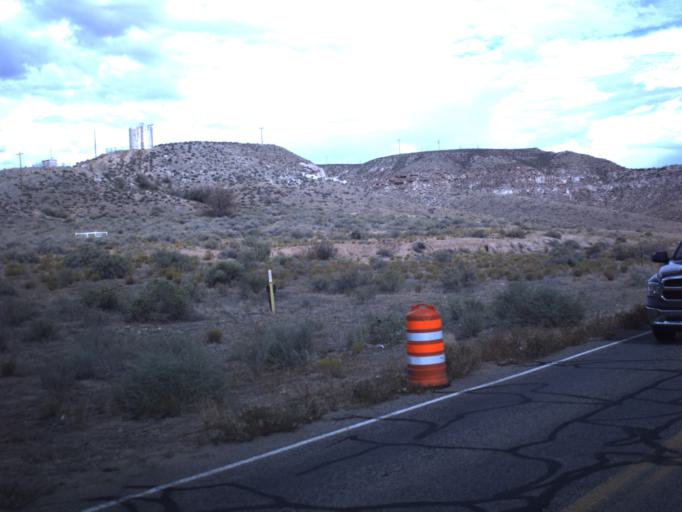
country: US
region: Utah
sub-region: San Juan County
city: Blanding
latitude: 37.2591
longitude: -109.2983
